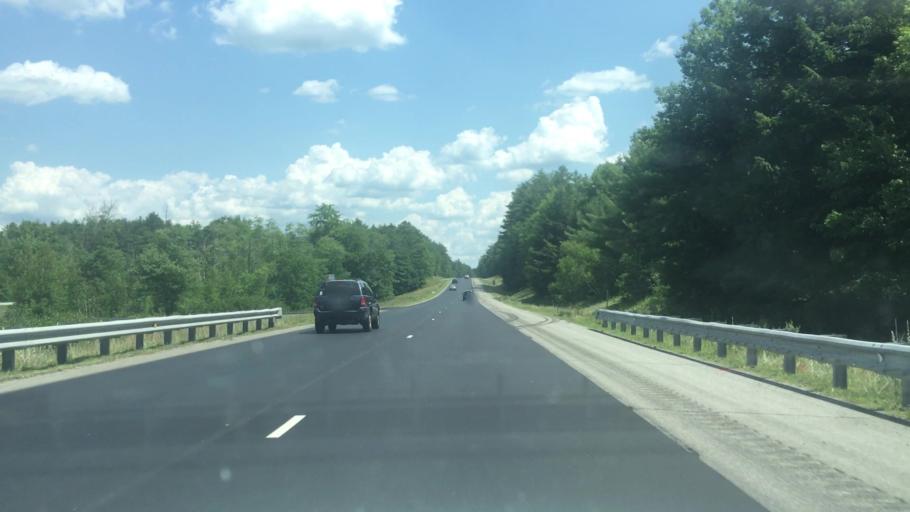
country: US
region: New Hampshire
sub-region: Merrimack County
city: Contoocook
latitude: 43.2663
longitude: -71.7691
